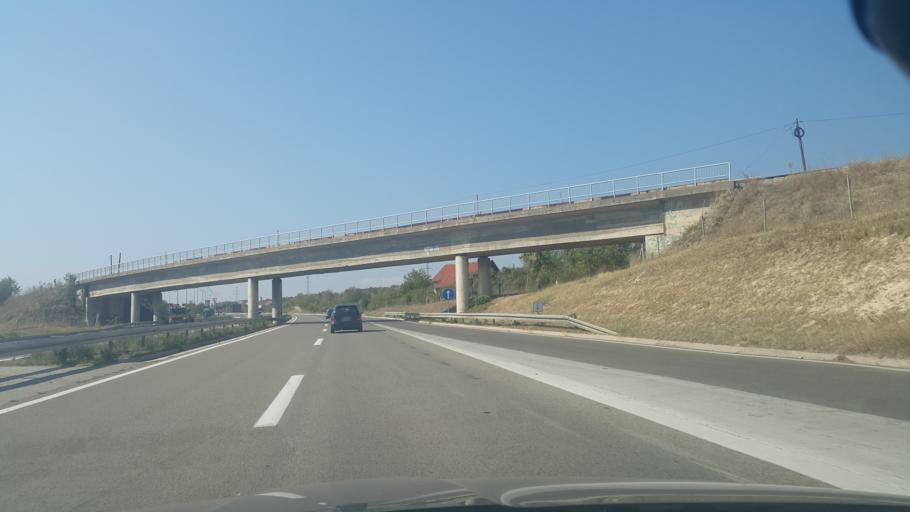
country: RS
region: Central Serbia
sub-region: Nisavski Okrug
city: Nis
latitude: 43.3412
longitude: 21.9323
